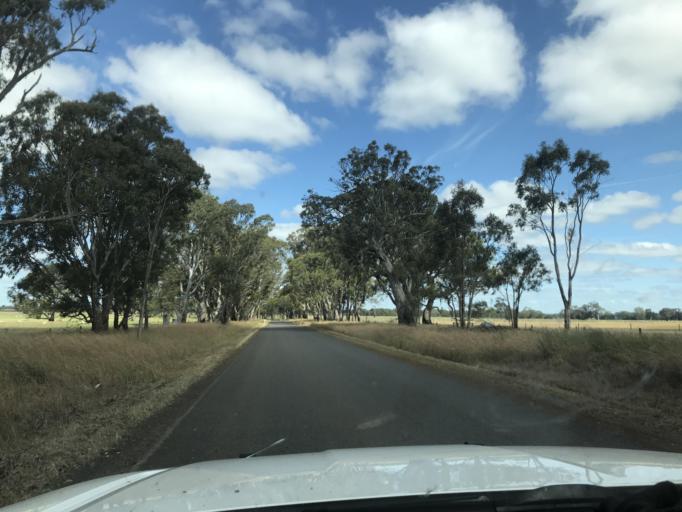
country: AU
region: South Australia
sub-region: Naracoorte and Lucindale
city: Naracoorte
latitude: -36.9895
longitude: 141.2819
